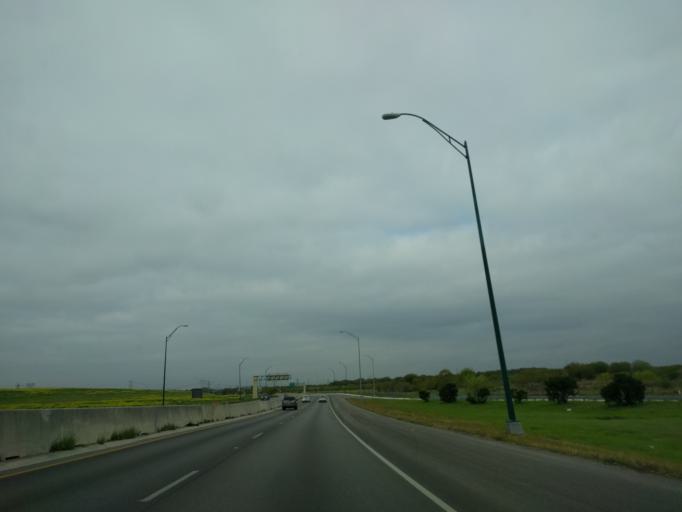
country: US
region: Texas
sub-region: Bexar County
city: Windcrest
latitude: 29.5466
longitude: -98.4392
